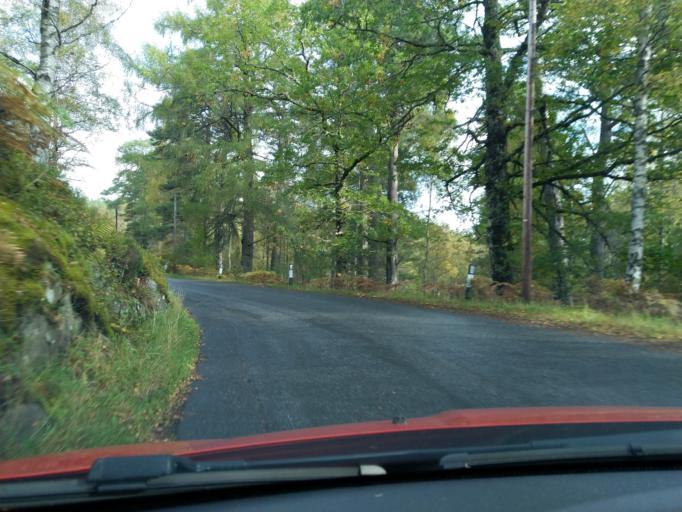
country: GB
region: Scotland
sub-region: Perth and Kinross
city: Aberfeldy
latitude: 56.7079
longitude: -4.0720
